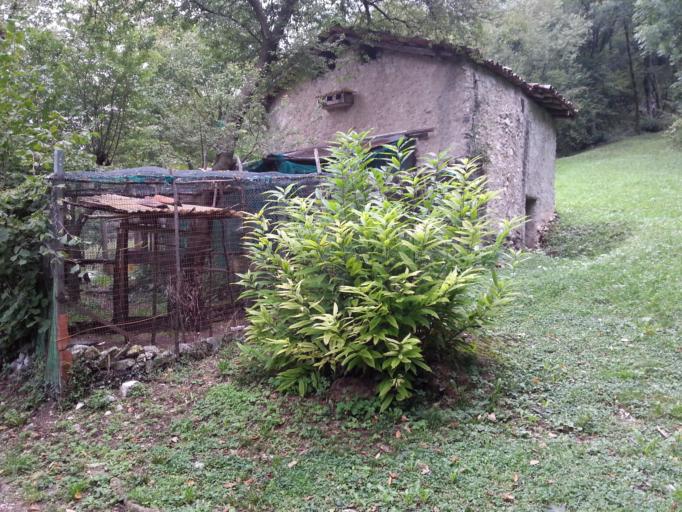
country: IT
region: Lombardy
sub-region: Provincia di Lecco
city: Ballabio
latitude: 45.8646
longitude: 9.4306
